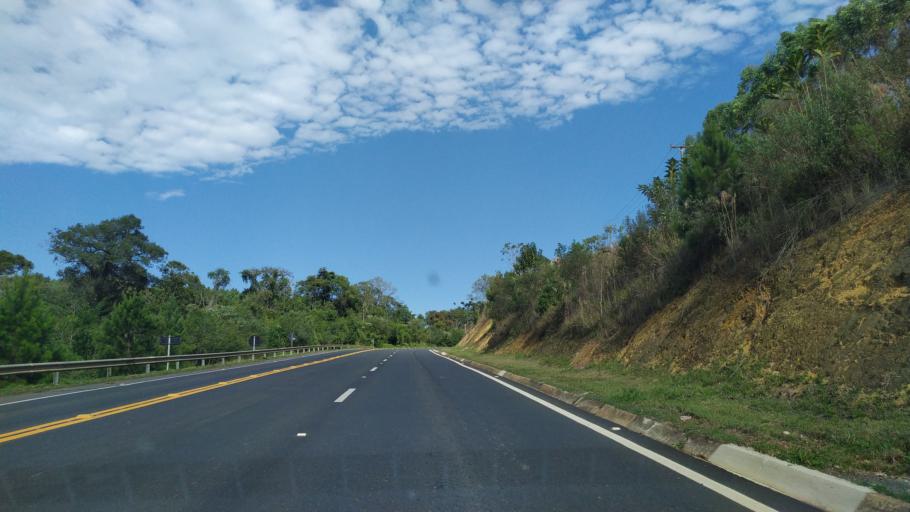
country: BR
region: Parana
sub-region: Telemaco Borba
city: Telemaco Borba
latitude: -24.2981
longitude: -50.7038
